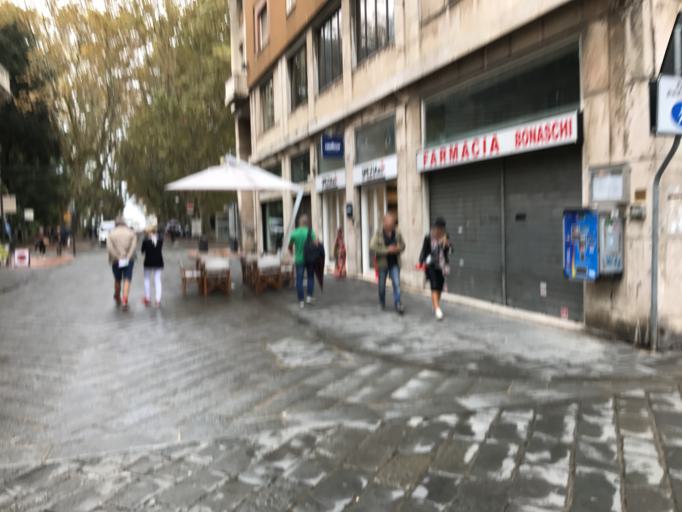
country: IT
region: Liguria
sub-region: Provincia di La Spezia
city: La Spezia
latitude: 44.1037
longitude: 9.8222
